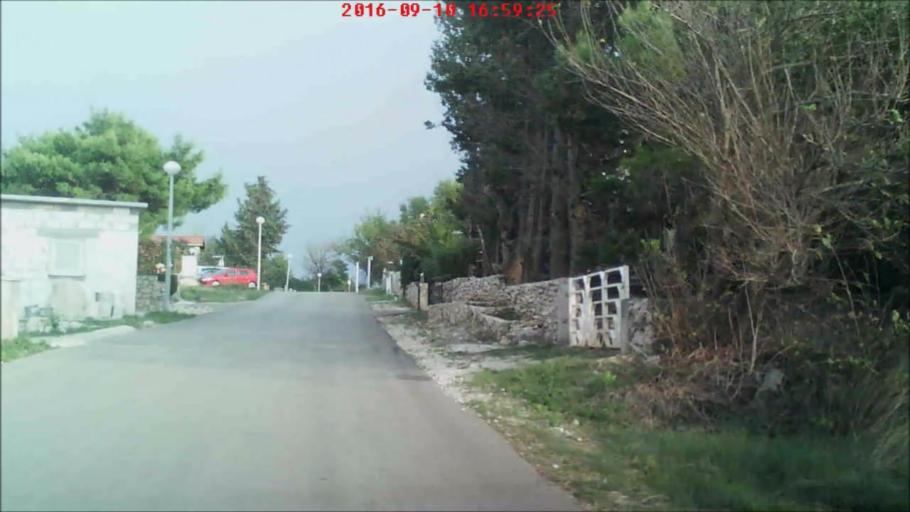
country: HR
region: Zadarska
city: Vir
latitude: 44.3126
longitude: 15.0538
